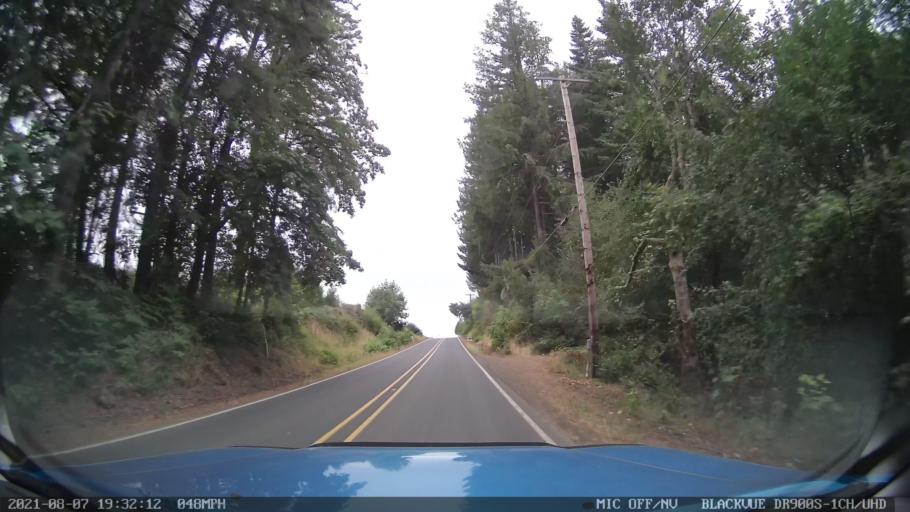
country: US
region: Oregon
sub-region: Linn County
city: Lyons
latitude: 44.8982
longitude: -122.6410
